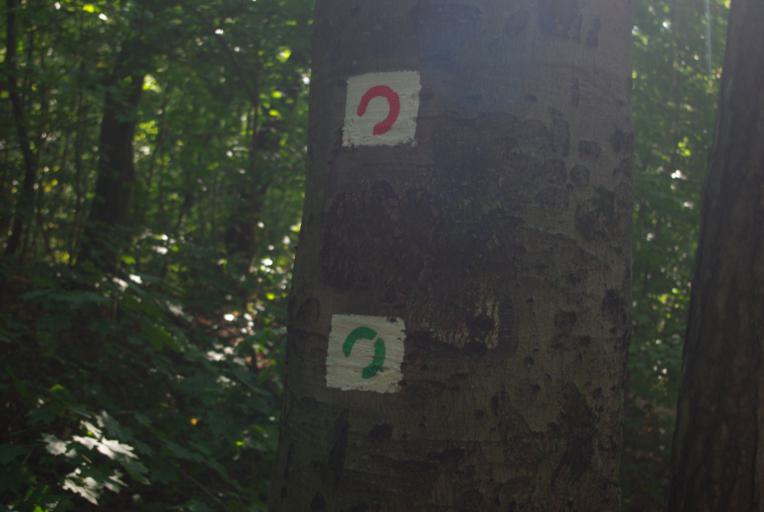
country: HU
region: Budapest
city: Budapest II. keruelet
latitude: 47.5416
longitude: 18.9870
